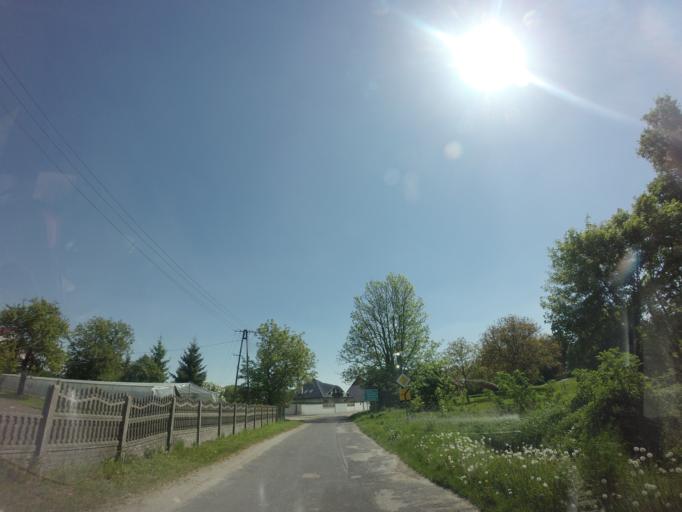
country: PL
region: West Pomeranian Voivodeship
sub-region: Powiat mysliborski
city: Nowogrodek Pomorski
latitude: 52.9129
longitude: 15.0265
